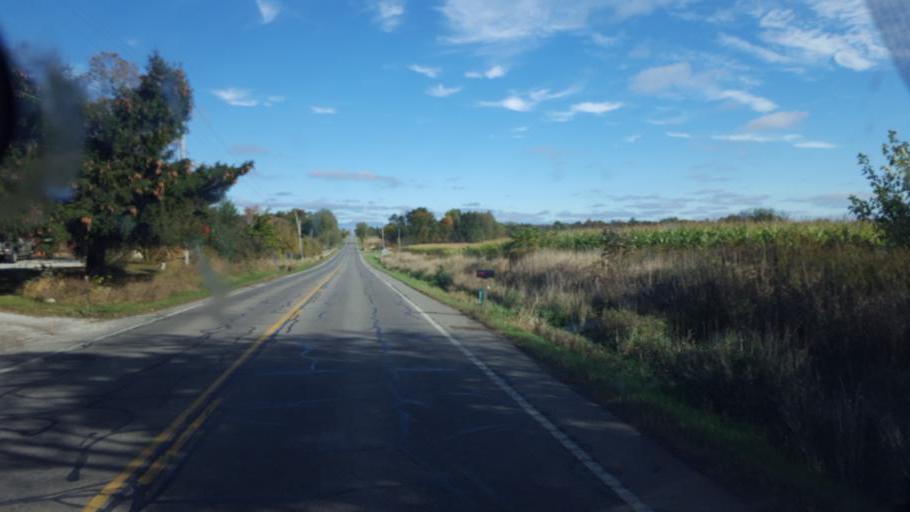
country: US
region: Ohio
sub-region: Huron County
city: Greenwich
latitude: 40.9145
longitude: -82.4991
